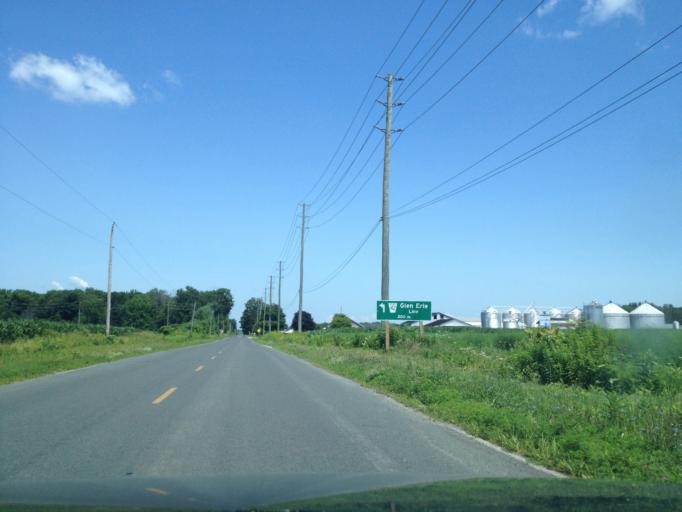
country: CA
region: Ontario
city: Aylmer
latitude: 42.6349
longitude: -80.7207
